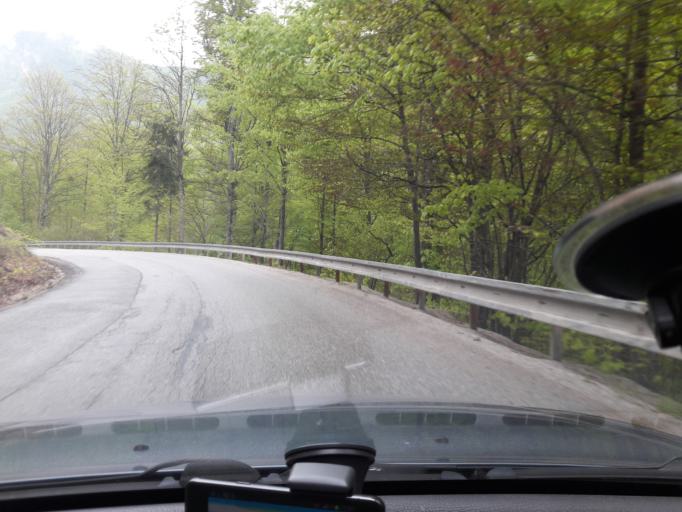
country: SK
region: Banskobystricky
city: Revuca
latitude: 48.7622
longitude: 20.0838
